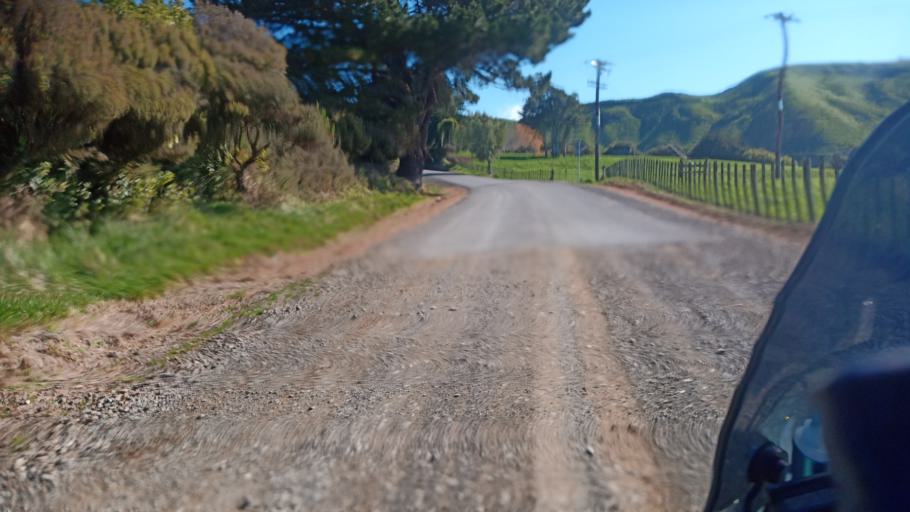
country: NZ
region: Gisborne
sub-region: Gisborne District
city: Gisborne
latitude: -39.1544
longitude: 177.9135
